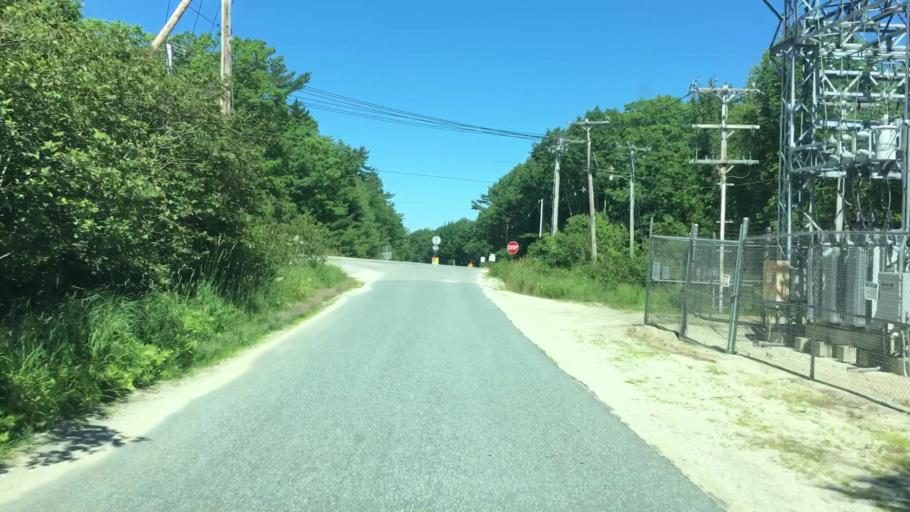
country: US
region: Maine
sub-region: Hancock County
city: Sedgwick
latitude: 44.3422
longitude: -68.6732
